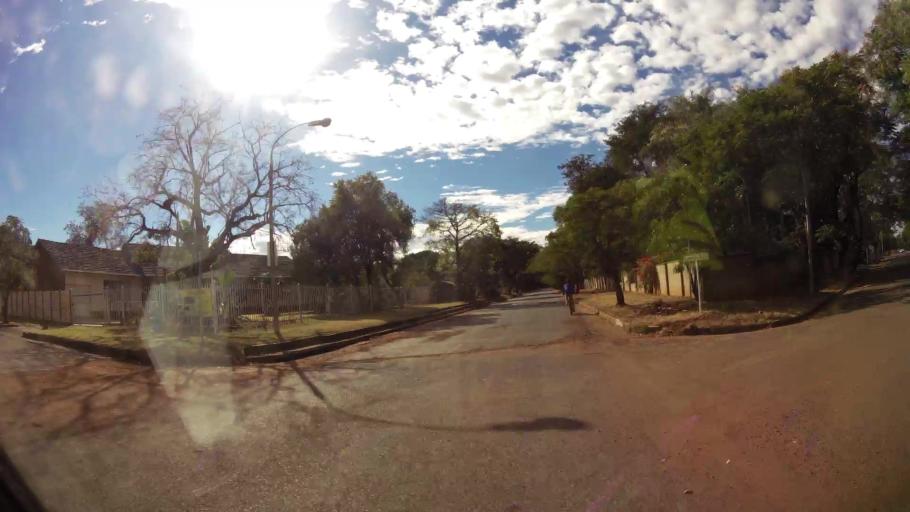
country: ZA
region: Limpopo
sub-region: Waterberg District Municipality
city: Warmbaths
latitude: -24.8785
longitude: 28.2845
